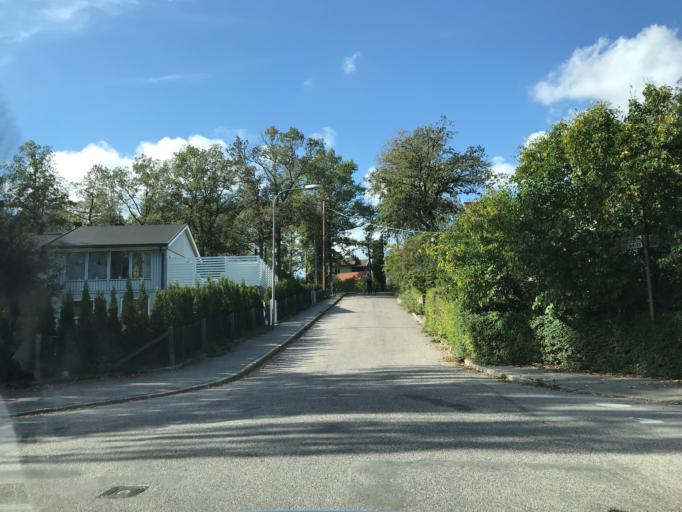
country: SE
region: Stockholm
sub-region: Huddinge Kommun
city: Segeltorp
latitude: 59.2755
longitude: 17.9689
